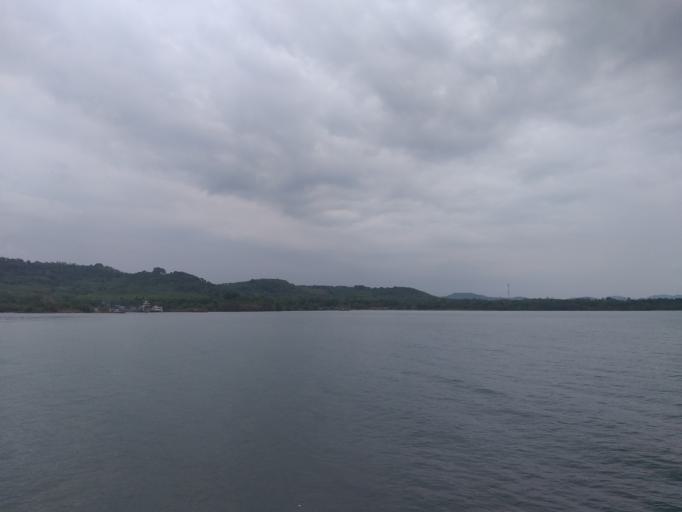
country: TH
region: Trat
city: Laem Ngop
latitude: 12.1784
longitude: 102.3006
